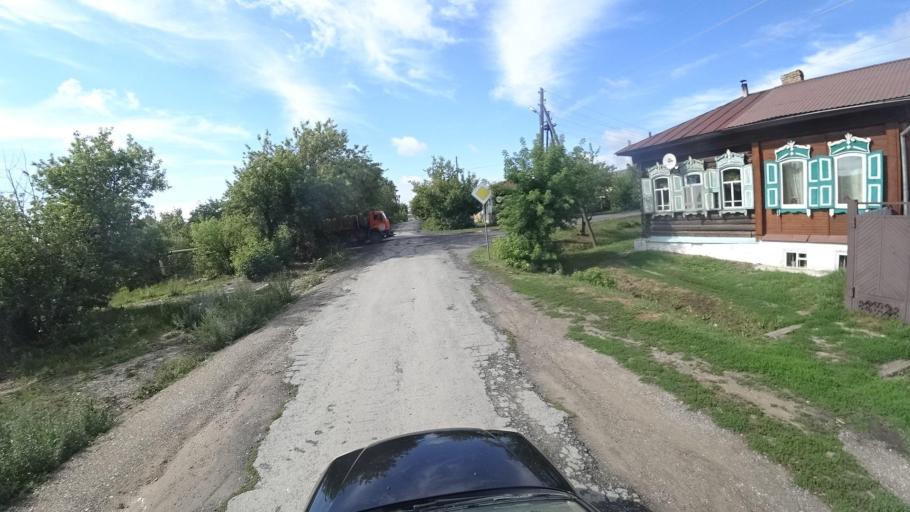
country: RU
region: Sverdlovsk
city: Kamyshlov
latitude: 56.8387
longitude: 62.7063
